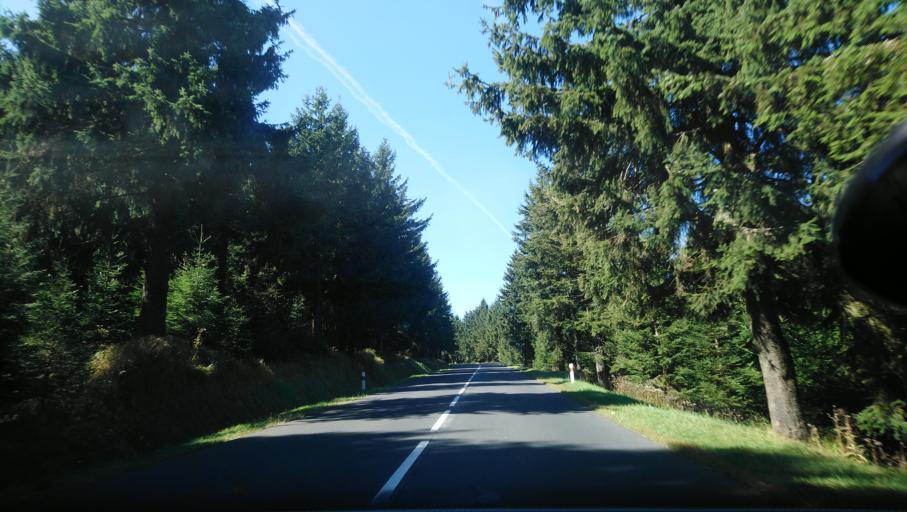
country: DE
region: Saxony
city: Kurort Oberwiesenthal
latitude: 50.4035
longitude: 12.9548
